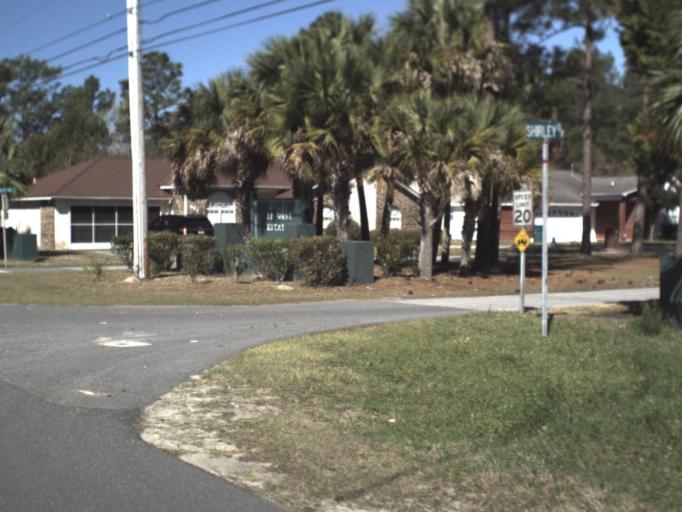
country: US
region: Florida
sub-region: Bay County
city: Callaway
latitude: 30.1528
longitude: -85.5481
